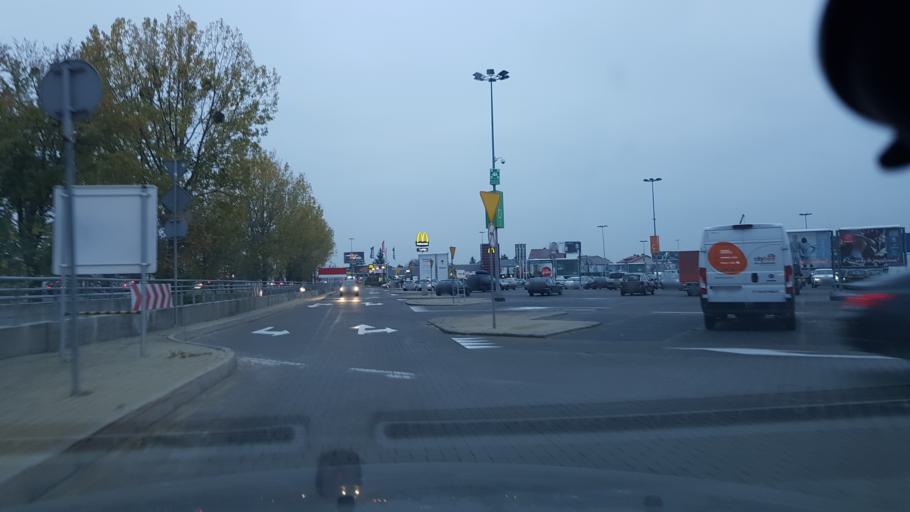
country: PL
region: Masovian Voivodeship
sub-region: Powiat pruszkowski
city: Nowe Grocholice
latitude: 52.1344
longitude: 20.8984
